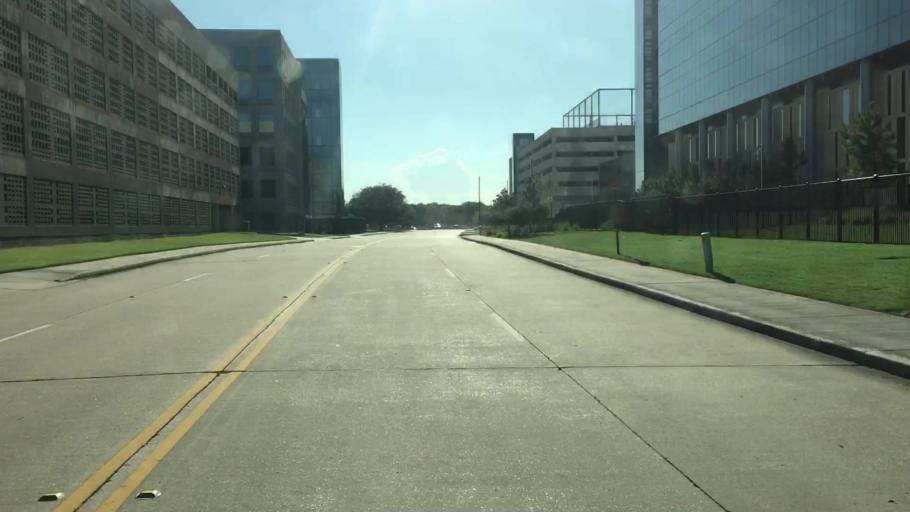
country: US
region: Texas
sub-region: Harris County
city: Bunker Hill Village
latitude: 29.7416
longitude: -95.5620
